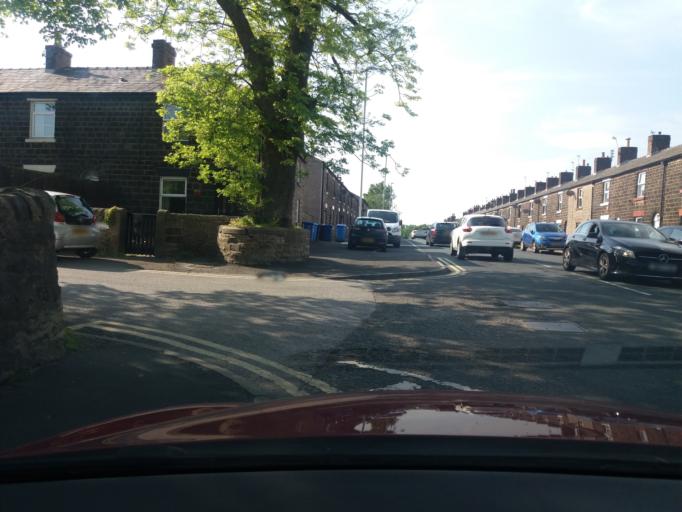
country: GB
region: England
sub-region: Blackburn with Darwen
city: Darwen
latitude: 53.6986
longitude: -2.5448
